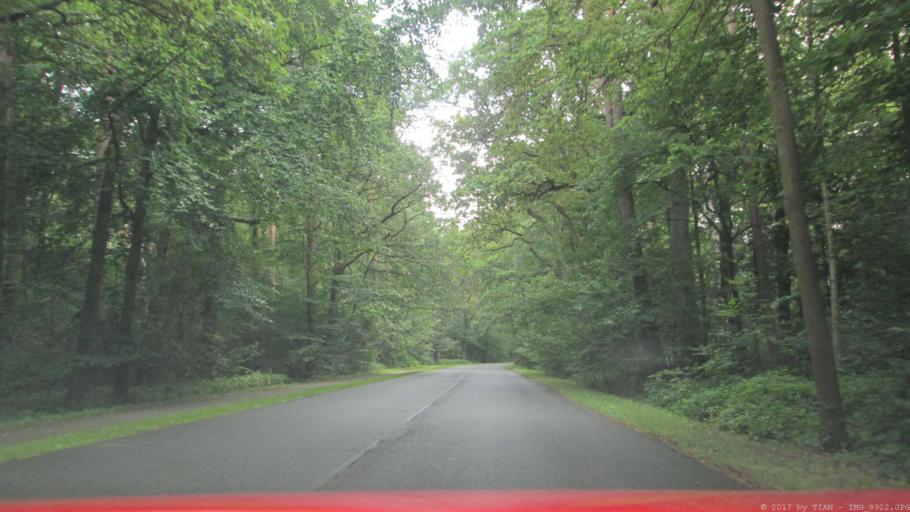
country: DE
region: Lower Saxony
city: Wolfsburg
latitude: 52.4573
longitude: 10.8049
